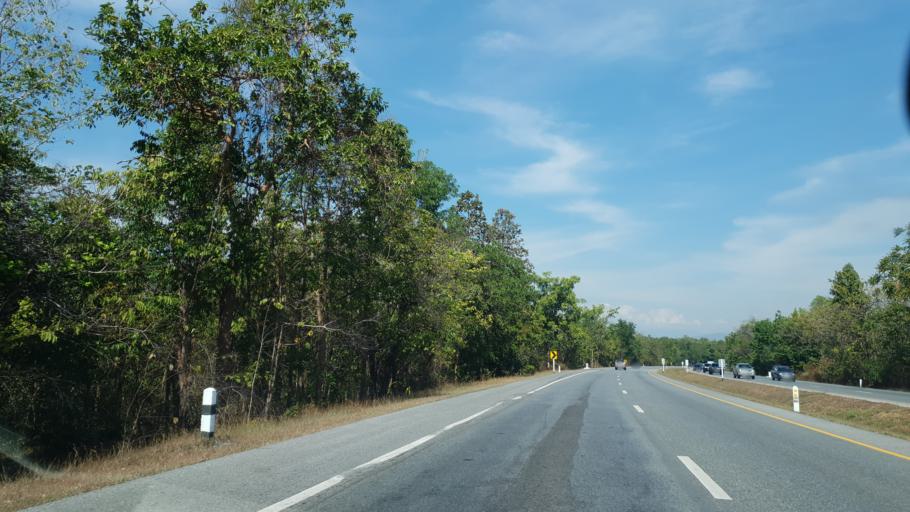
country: TH
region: Uttaradit
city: Thong Saen Khan
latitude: 17.4248
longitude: 100.2257
